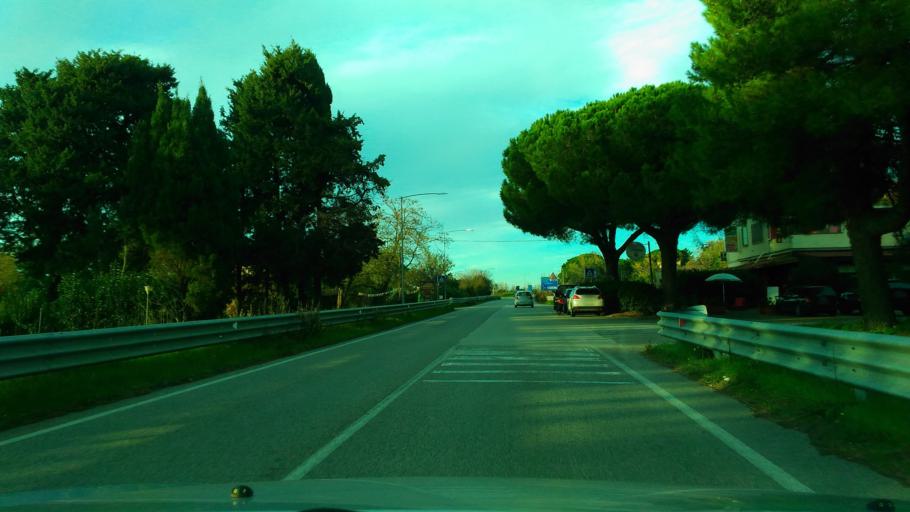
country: IT
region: Tuscany
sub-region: Provincia di Livorno
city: S.P. in Palazzi
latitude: 43.3460
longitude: 10.5042
